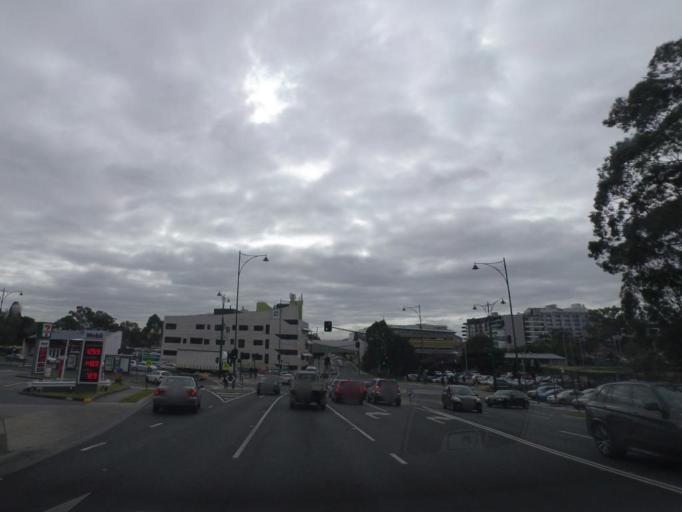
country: AU
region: Victoria
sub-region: Whitehorse
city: Box Hill
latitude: -37.8173
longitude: 145.1150
